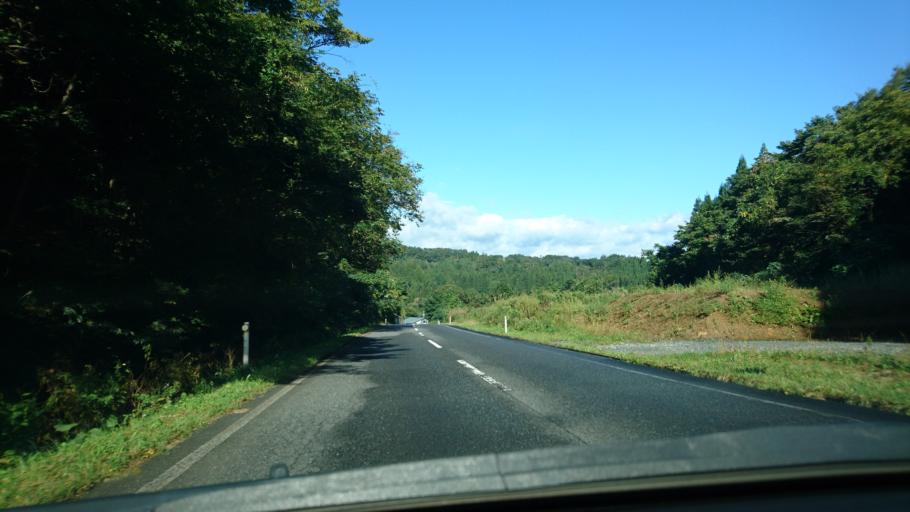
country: JP
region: Iwate
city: Ichinoseki
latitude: 39.0075
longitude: 141.0300
